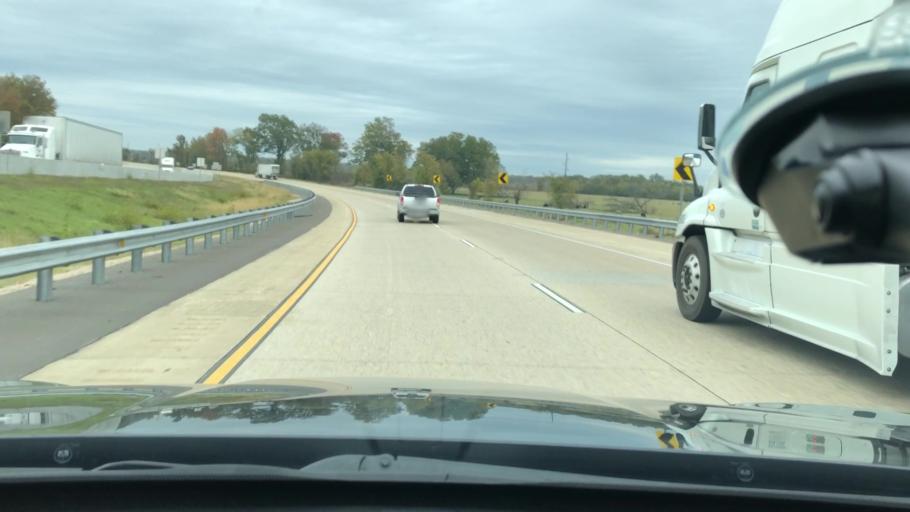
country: US
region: Arkansas
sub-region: Miller County
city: Texarkana
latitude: 33.5503
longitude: -93.8706
